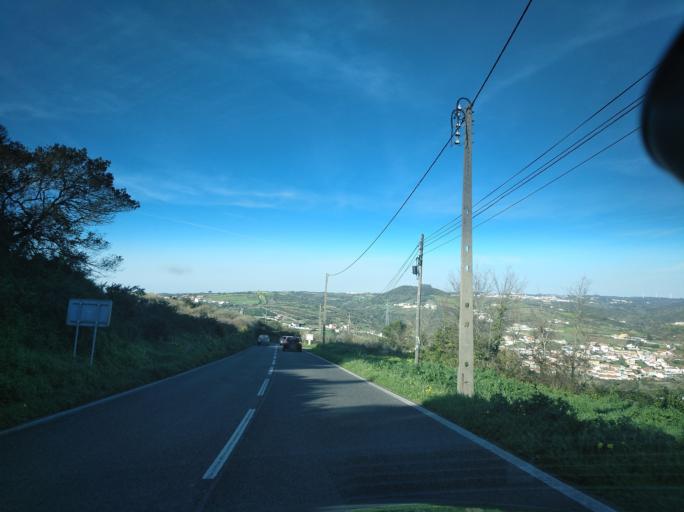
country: PT
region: Lisbon
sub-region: Sintra
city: Pero Pinheiro
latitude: 38.8800
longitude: -9.3297
